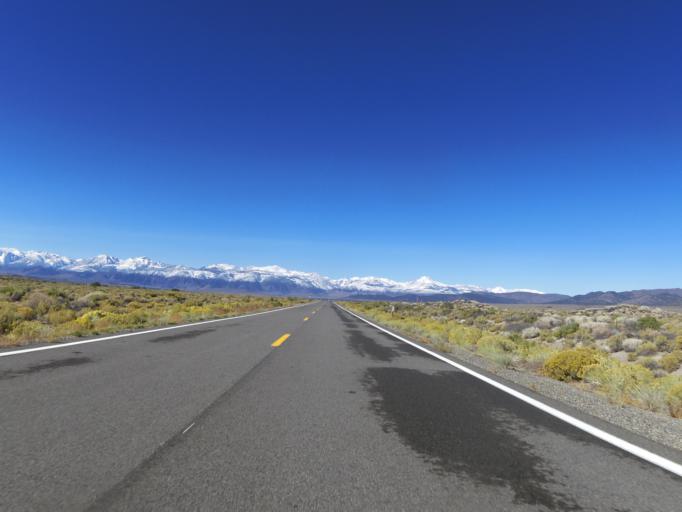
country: US
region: California
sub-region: Mono County
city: Bridgeport
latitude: 38.1160
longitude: -118.9356
